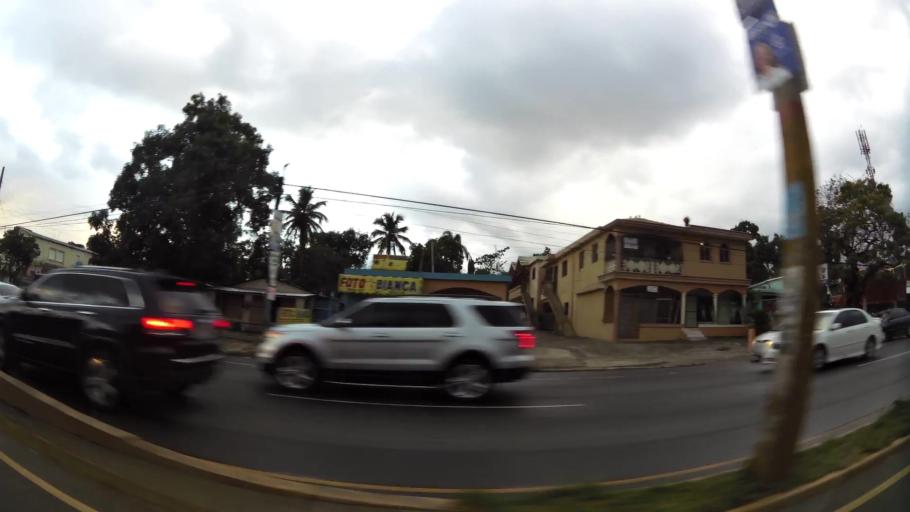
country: DO
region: Santo Domingo
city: Santo Domingo Oeste
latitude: 18.5678
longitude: -70.0911
